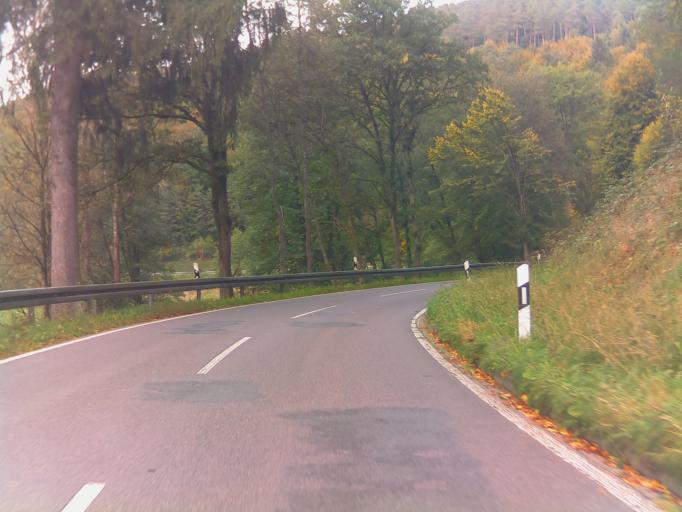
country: DE
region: Bavaria
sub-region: Regierungsbezirk Unterfranken
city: Kirchzell
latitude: 49.6147
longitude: 9.1453
